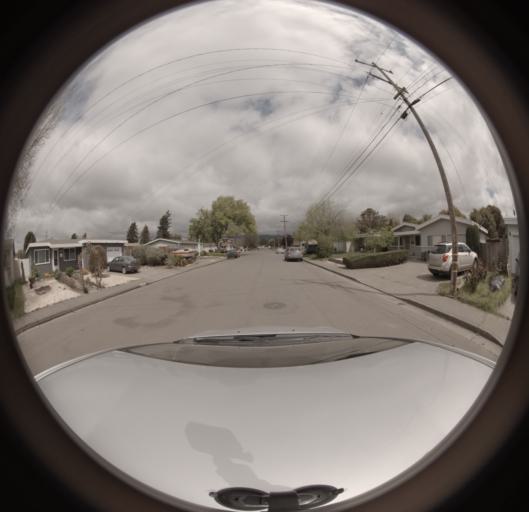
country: US
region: California
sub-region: Sonoma County
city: Petaluma
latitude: 38.2520
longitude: -122.6247
